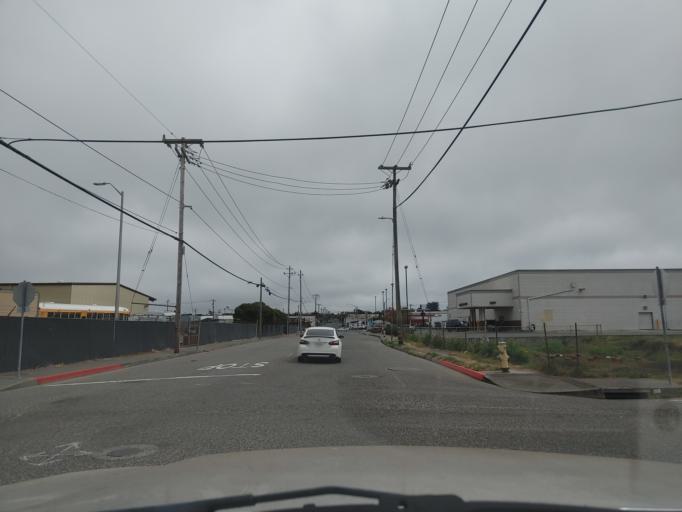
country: US
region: California
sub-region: Humboldt County
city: Eureka
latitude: 40.7941
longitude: -124.1791
